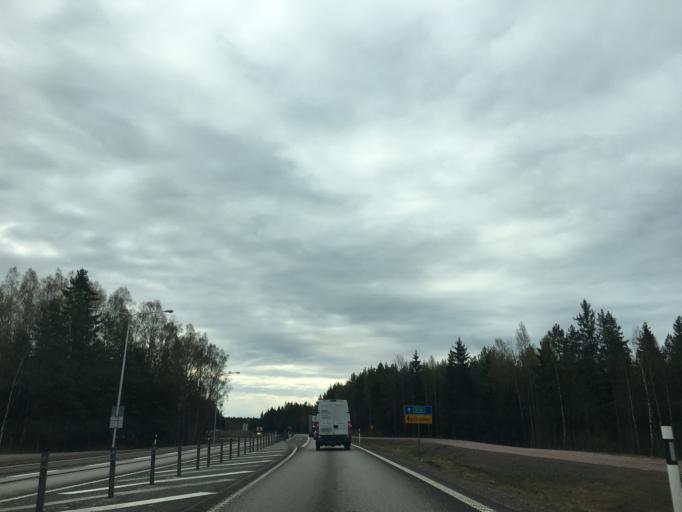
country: SE
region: Vaermland
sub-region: Kristinehamns Kommun
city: Kristinehamn
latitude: 59.3619
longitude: 14.0291
